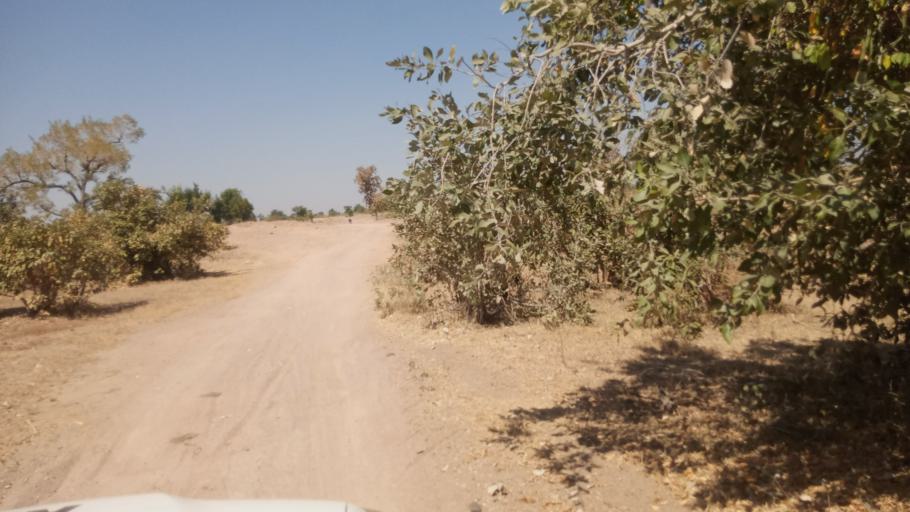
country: NG
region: Adamawa
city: Mayo Belwa
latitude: 9.0941
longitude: 12.0238
